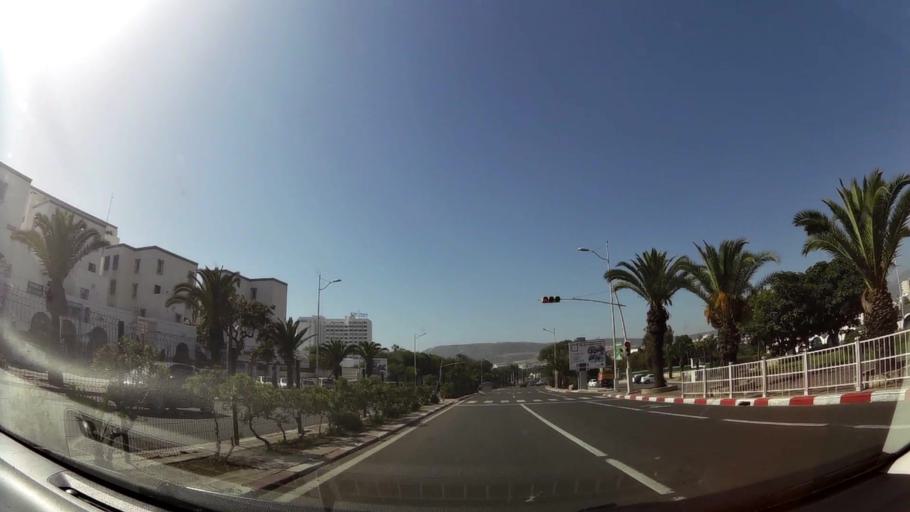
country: MA
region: Souss-Massa-Draa
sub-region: Agadir-Ida-ou-Tnan
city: Agadir
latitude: 30.4149
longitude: -9.5984
